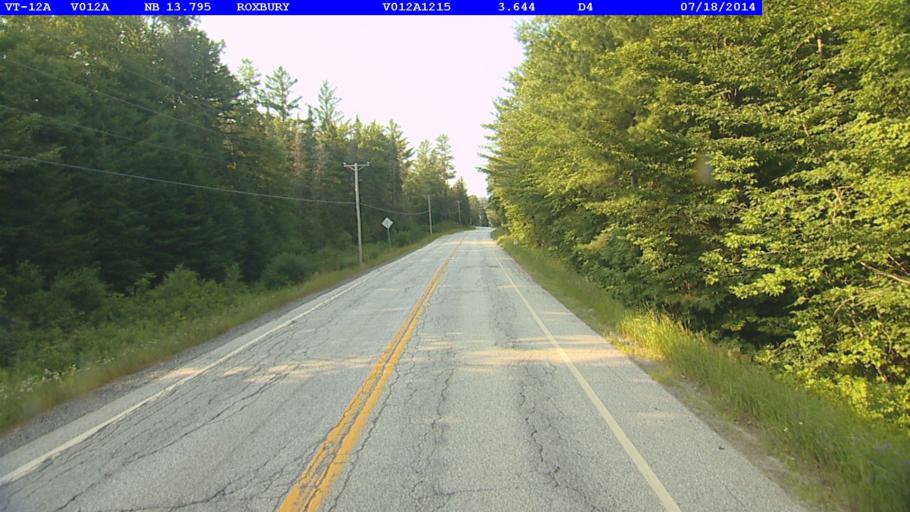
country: US
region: Vermont
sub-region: Washington County
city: Northfield
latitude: 44.0783
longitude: -72.7382
